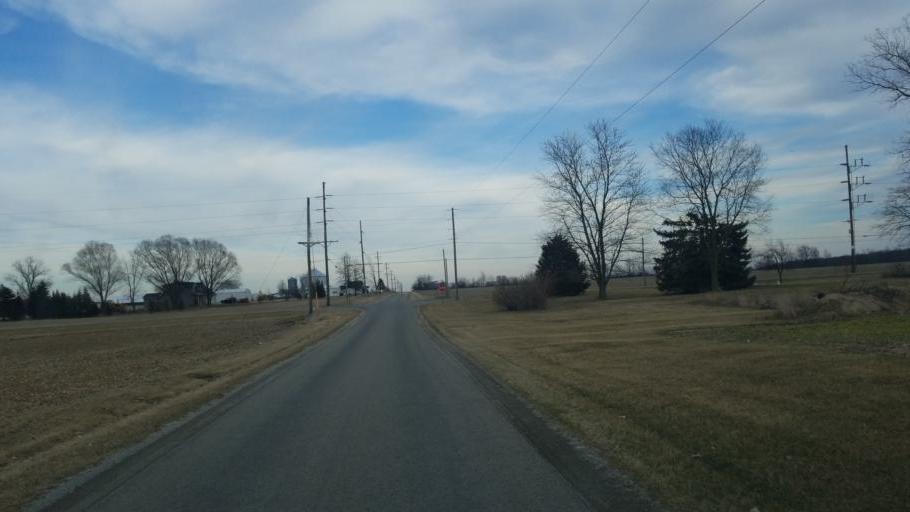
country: US
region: Ohio
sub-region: Defiance County
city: Hicksville
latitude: 41.3536
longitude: -84.7682
